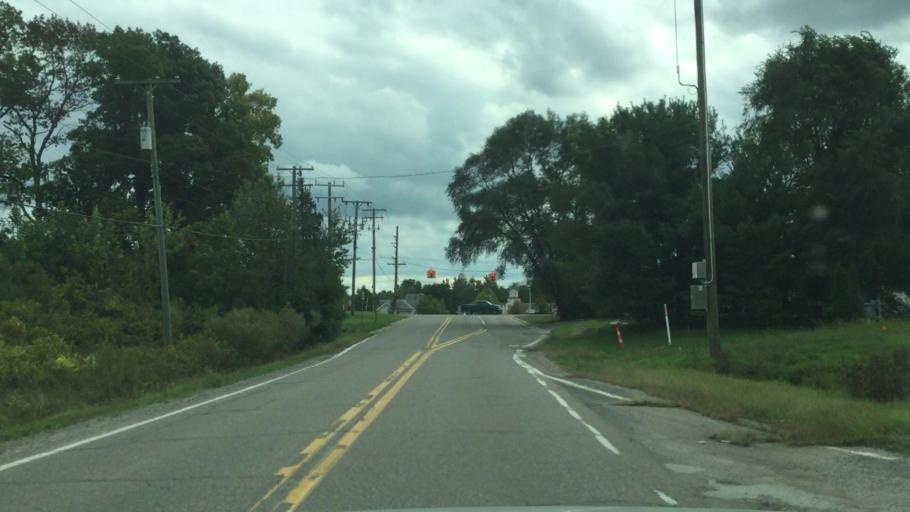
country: US
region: Michigan
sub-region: Livingston County
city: Brighton
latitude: 42.4646
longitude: -83.8337
